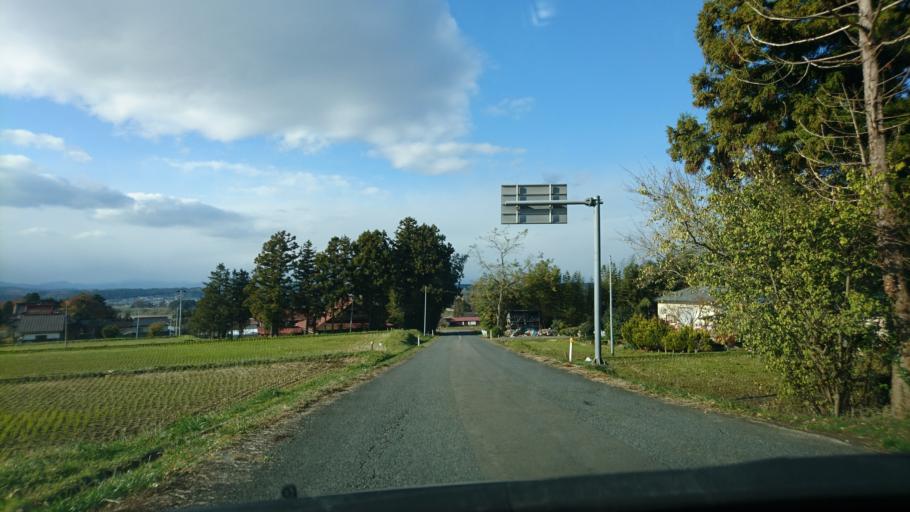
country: JP
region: Iwate
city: Mizusawa
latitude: 39.0336
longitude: 141.1549
